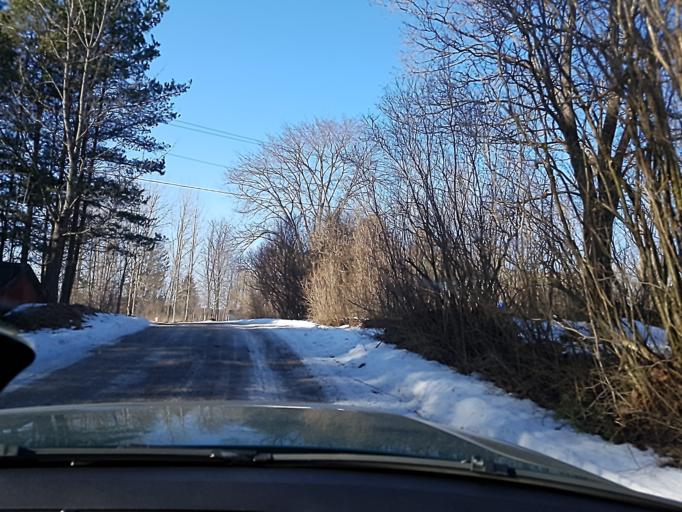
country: FI
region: Uusimaa
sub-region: Helsinki
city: Karjalohja
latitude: 60.2207
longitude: 23.6898
